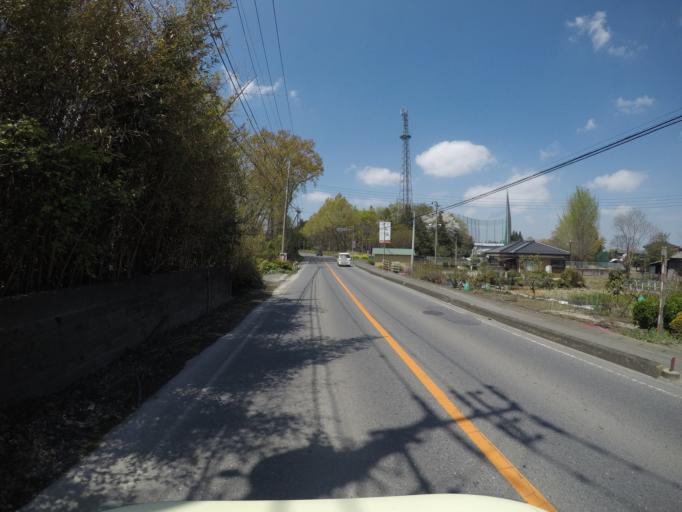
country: JP
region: Tochigi
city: Mibu
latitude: 36.3909
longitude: 139.8093
